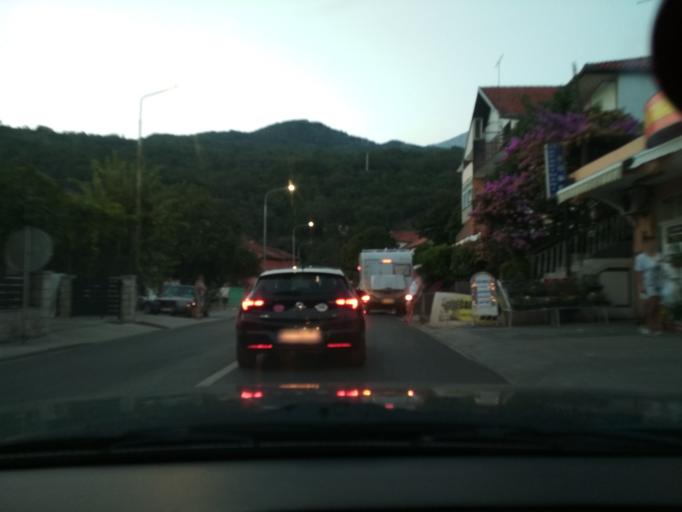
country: ME
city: Igalo
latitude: 42.4605
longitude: 18.5209
